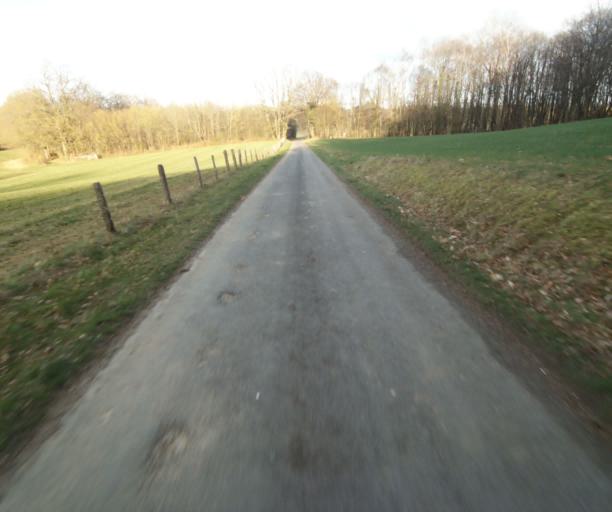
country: FR
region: Limousin
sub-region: Departement de la Correze
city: Uzerche
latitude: 45.3685
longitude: 1.5778
